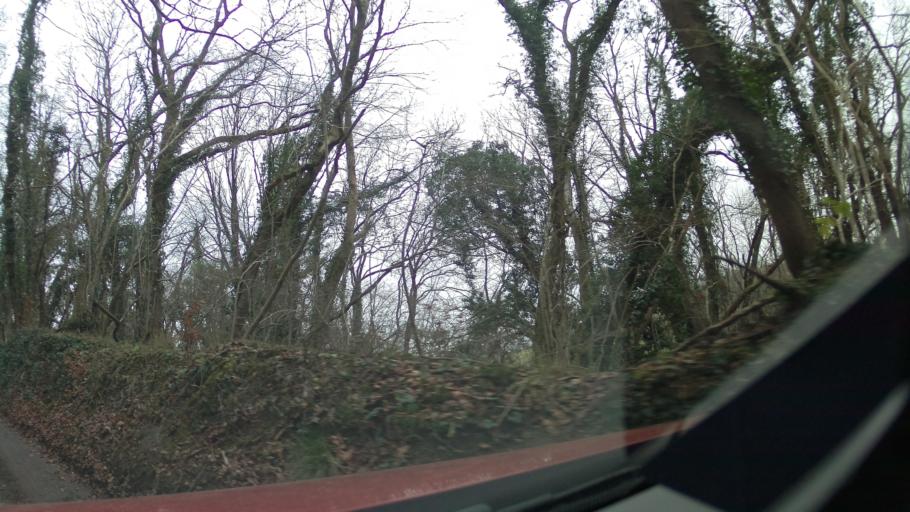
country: GB
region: England
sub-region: Wiltshire
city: Biddestone
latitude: 51.4704
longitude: -2.2316
